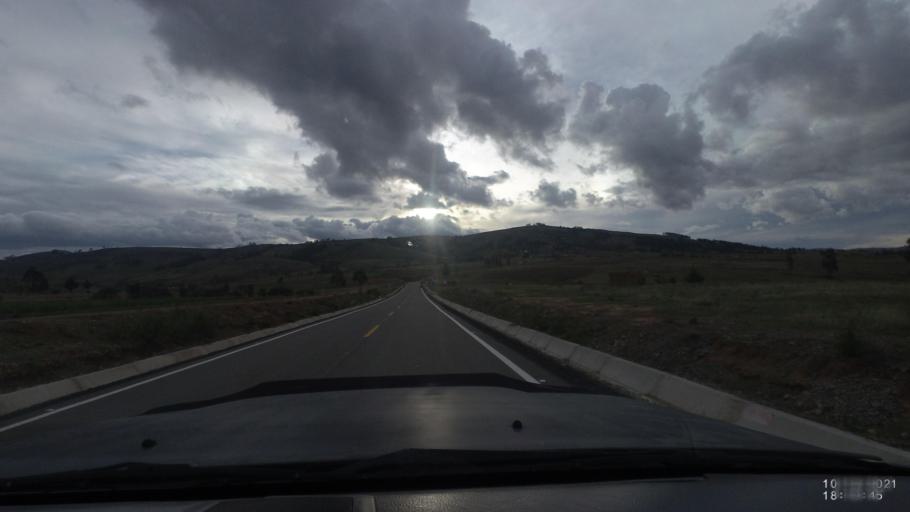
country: BO
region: Cochabamba
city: Tarata
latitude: -17.7848
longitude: -65.9603
